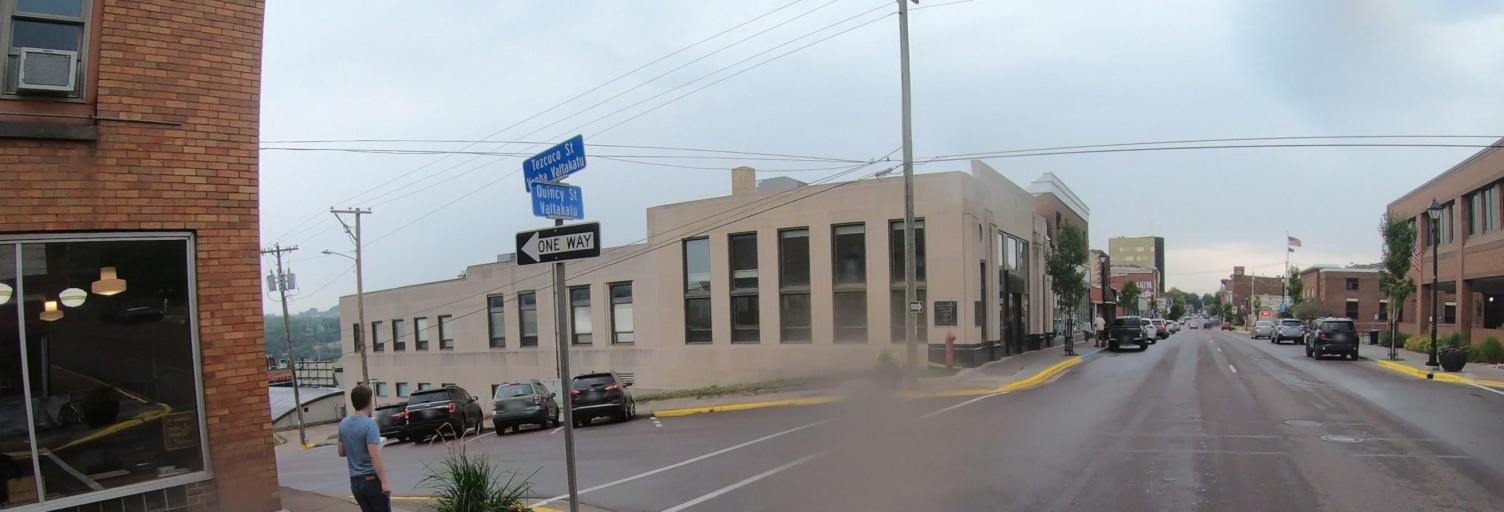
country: US
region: Michigan
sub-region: Houghton County
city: Hancock
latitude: 47.1269
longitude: -88.5805
